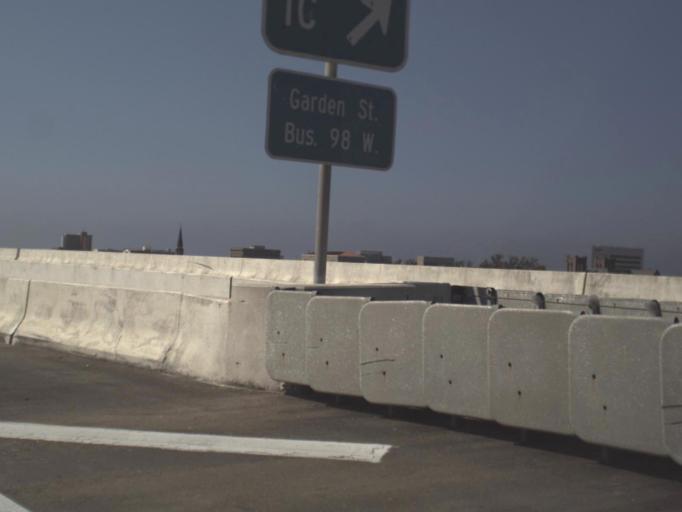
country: US
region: Florida
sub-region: Escambia County
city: Pensacola
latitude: 30.4197
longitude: -87.2137
